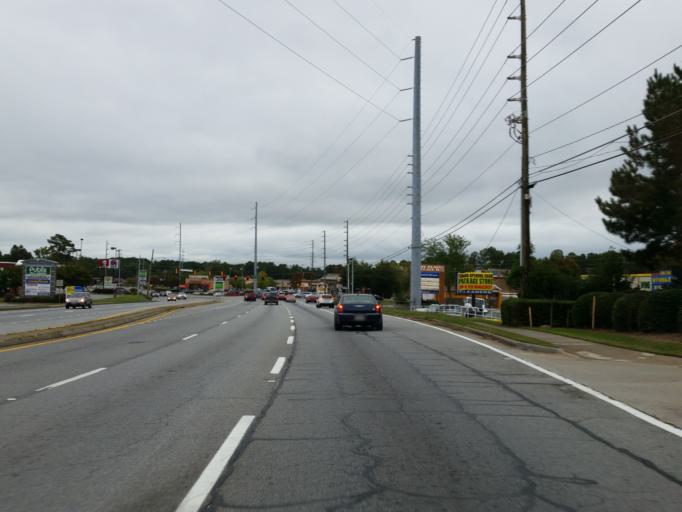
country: US
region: Georgia
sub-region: Fulton County
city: Roswell
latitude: 34.0656
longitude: -84.4245
